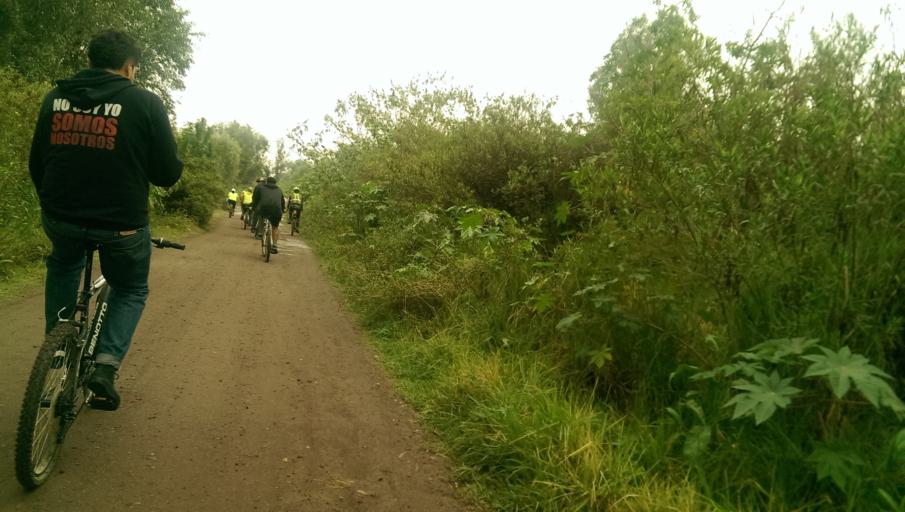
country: MX
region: Mexico City
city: Xochimilco
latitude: 19.2824
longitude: -99.0701
